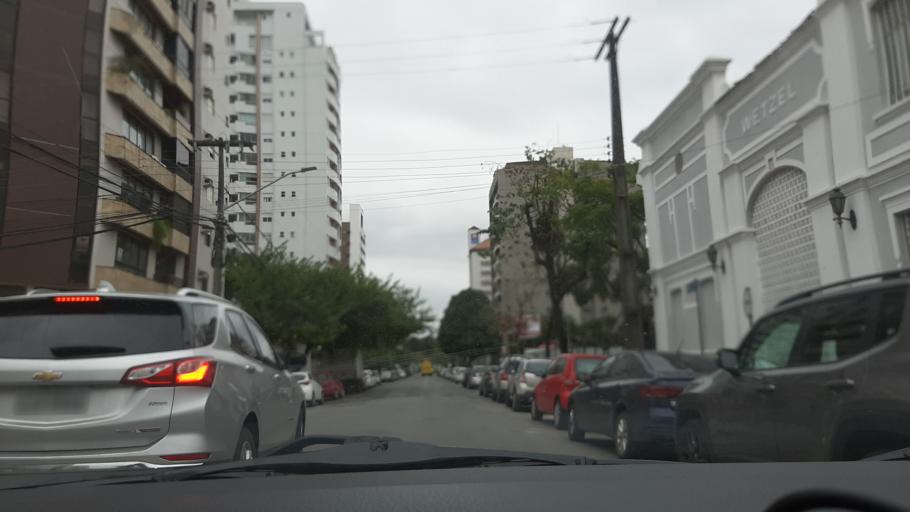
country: BR
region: Santa Catarina
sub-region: Joinville
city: Joinville
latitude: -26.3052
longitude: -48.8498
